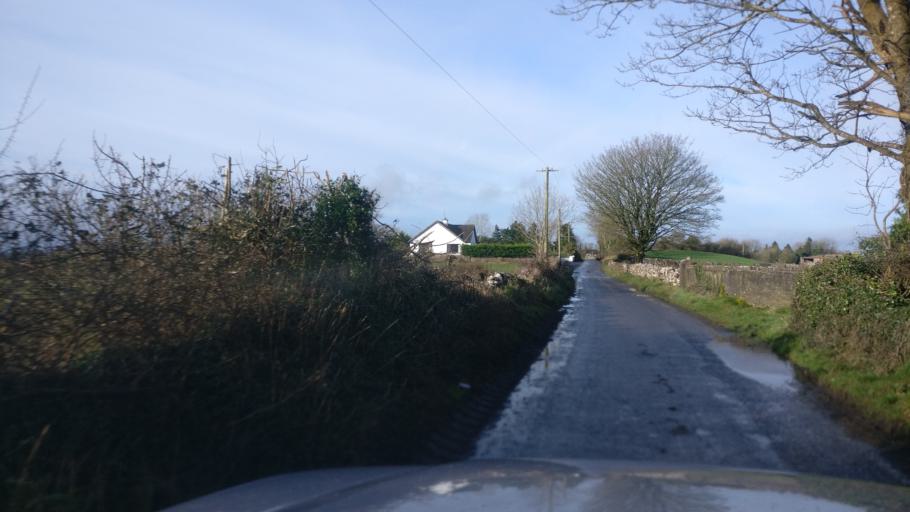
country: IE
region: Connaught
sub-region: County Galway
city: Loughrea
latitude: 53.1955
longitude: -8.6227
